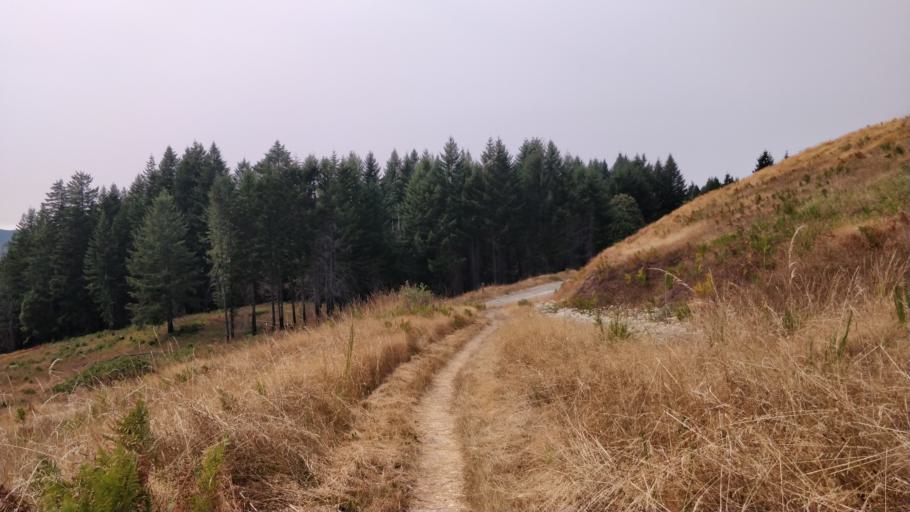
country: US
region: California
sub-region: Humboldt County
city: Westhaven-Moonstone
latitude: 41.2032
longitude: -123.9515
